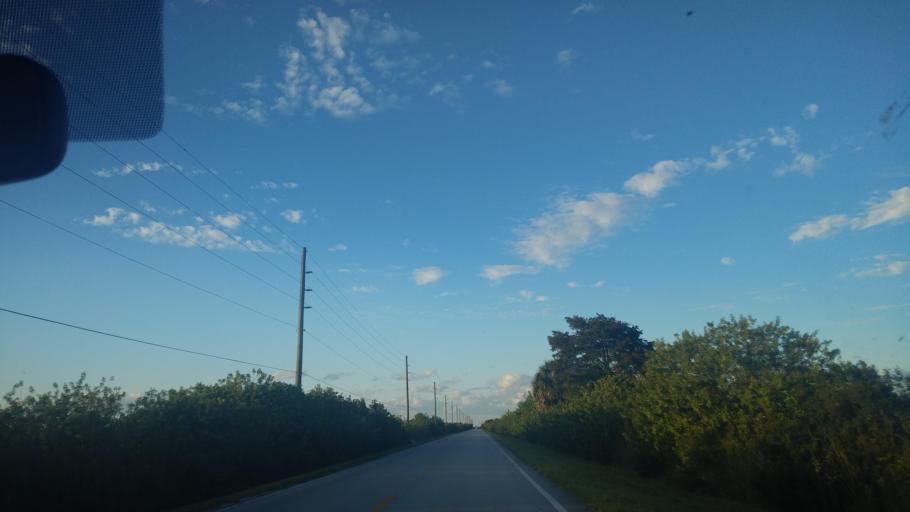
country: US
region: Florida
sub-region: Indian River County
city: Fellsmere
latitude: 27.6876
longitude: -80.6430
